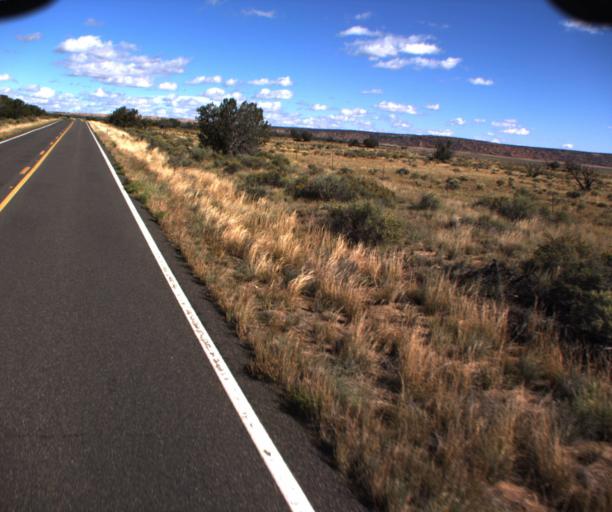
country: US
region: Arizona
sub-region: Apache County
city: Saint Johns
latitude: 34.7708
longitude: -109.2404
